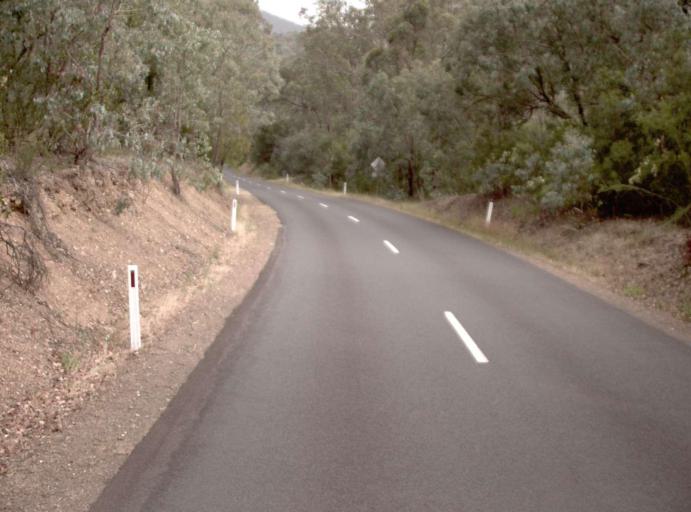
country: AU
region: Victoria
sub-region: Wellington
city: Heyfield
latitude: -37.7500
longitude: 146.6690
